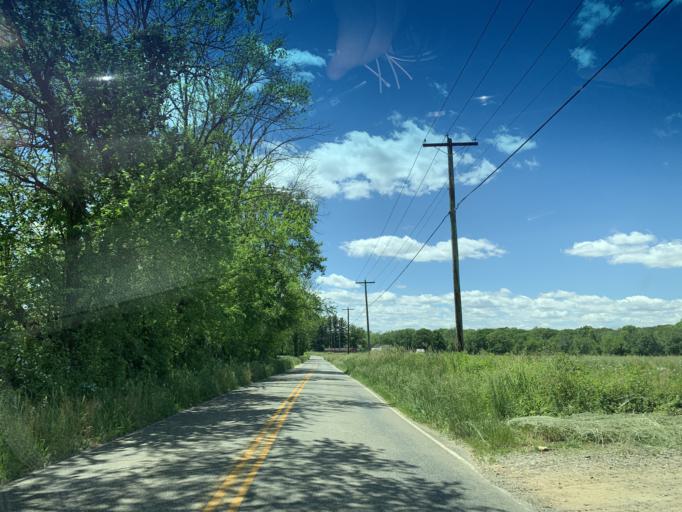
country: US
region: Maryland
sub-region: Cecil County
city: Rising Sun
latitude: 39.6926
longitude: -75.9998
